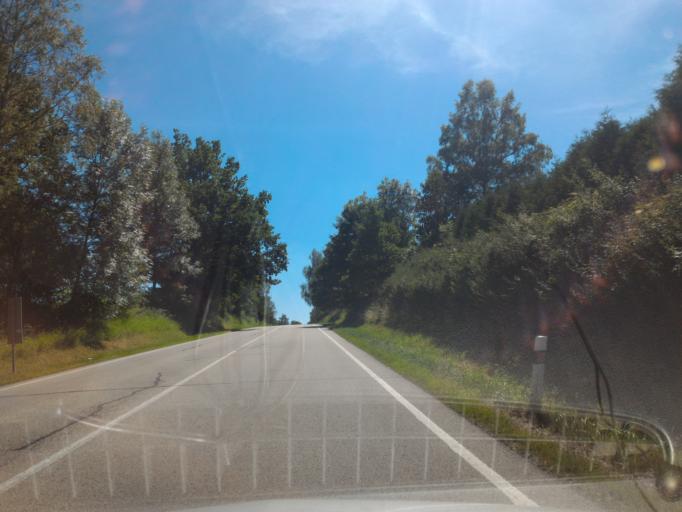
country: CZ
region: Vysocina
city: Dolni Cerekev
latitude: 49.3285
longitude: 15.4835
